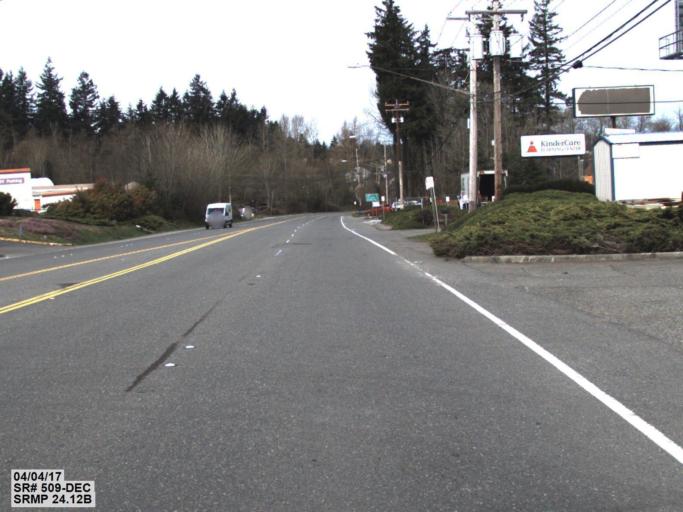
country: US
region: Washington
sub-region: King County
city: Normandy Park
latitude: 47.4408
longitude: -122.3258
